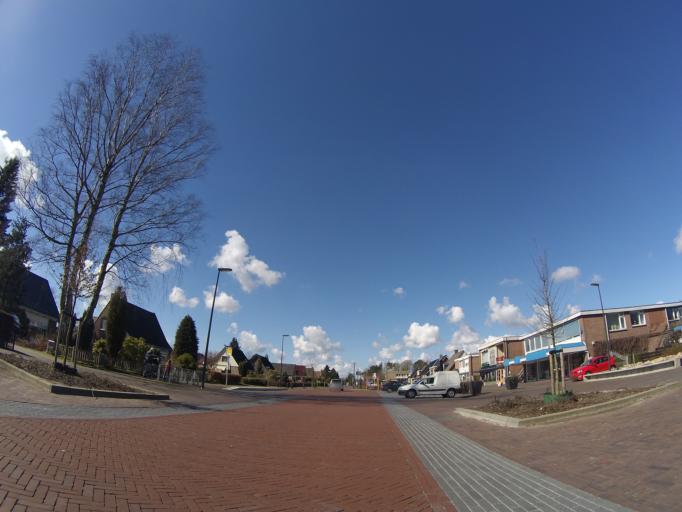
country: NL
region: Drenthe
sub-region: Gemeente Emmen
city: Emmen
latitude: 52.7730
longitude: 6.9598
